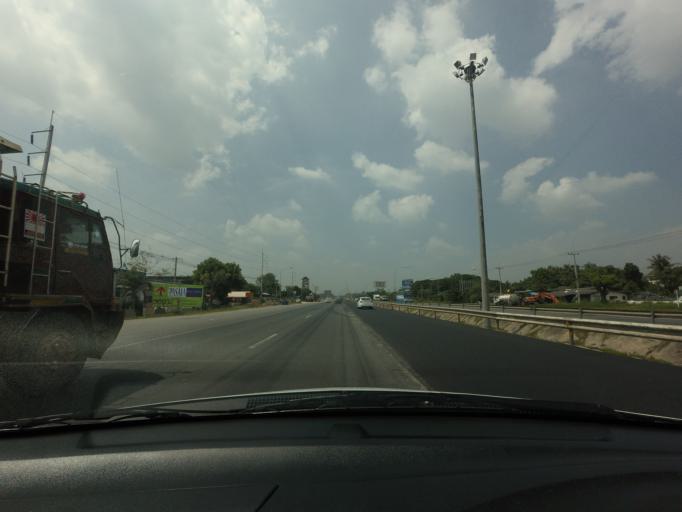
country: TH
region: Nakhon Ratchasima
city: Pak Chong
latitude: 14.6611
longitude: 101.3973
